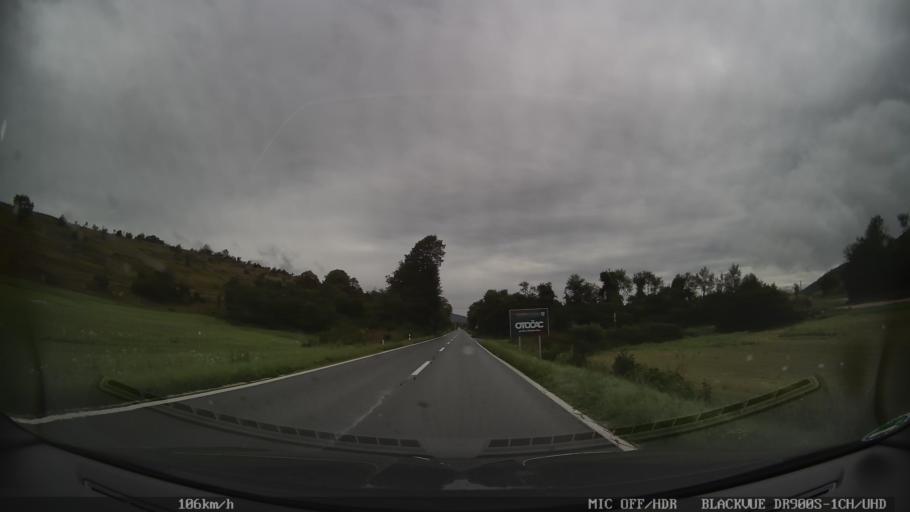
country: HR
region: Licko-Senjska
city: Brinje
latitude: 44.9526
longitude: 15.1095
